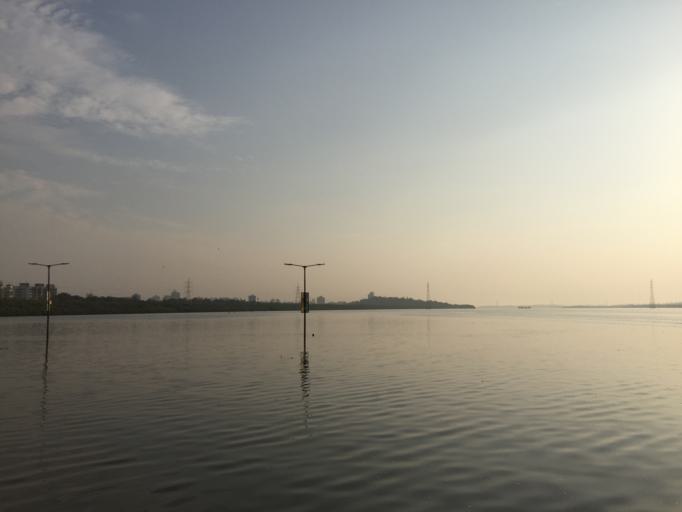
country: IN
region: Maharashtra
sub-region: Mumbai Suburban
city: Borivli
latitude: 19.2351
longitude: 72.8215
